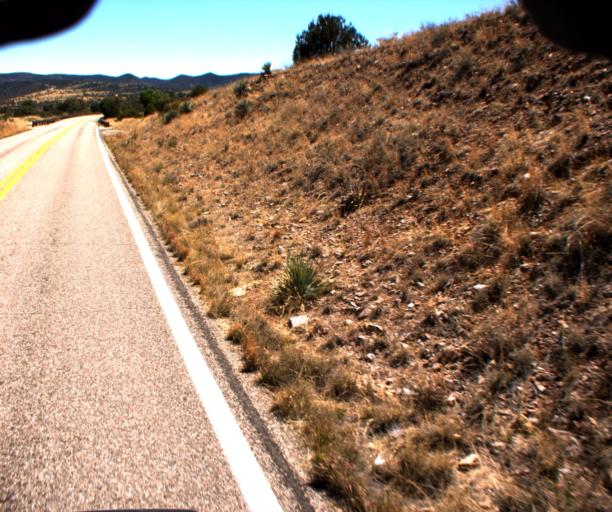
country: US
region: Arizona
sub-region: Cochise County
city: Sierra Vista
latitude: 31.5108
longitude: -110.4964
